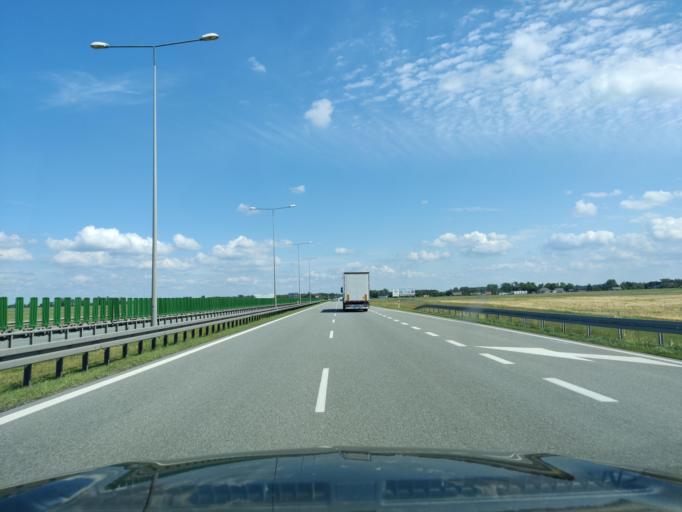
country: PL
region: Greater Poland Voivodeship
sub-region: Powiat slupecki
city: Slupca
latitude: 52.2512
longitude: 17.8315
